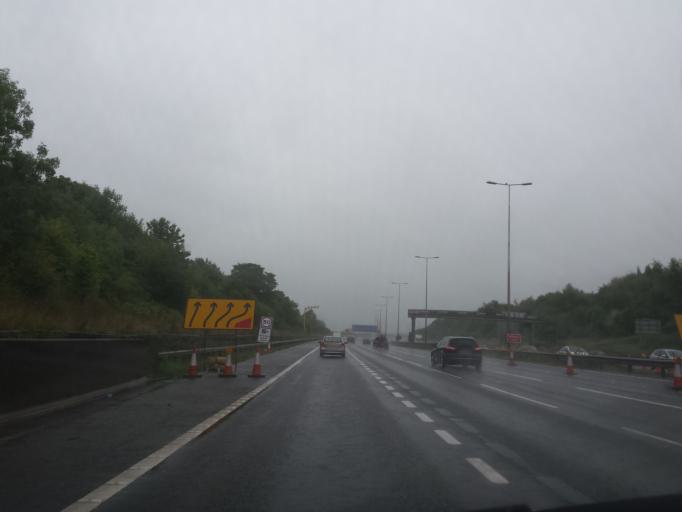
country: GB
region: England
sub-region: Leicestershire
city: Enderby
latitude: 52.6110
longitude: -1.1996
